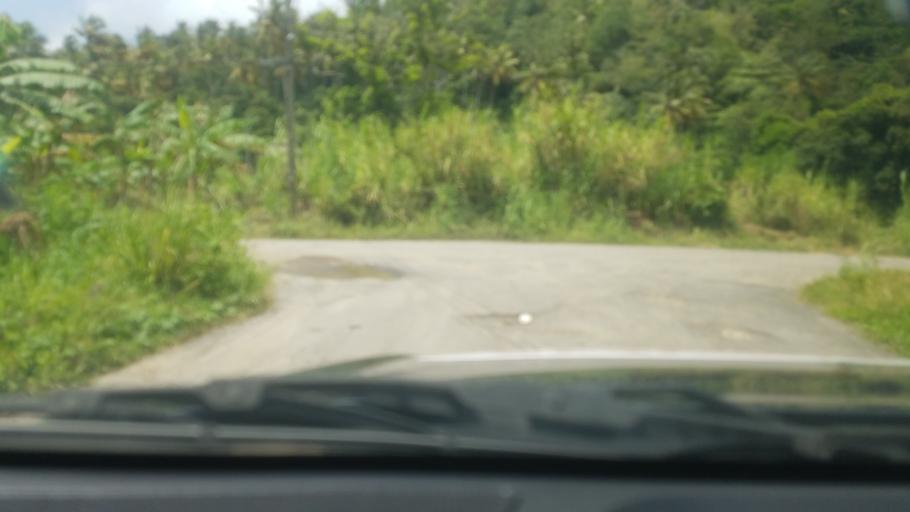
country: LC
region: Micoud Quarter
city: Micoud
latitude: 13.7977
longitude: -60.9458
